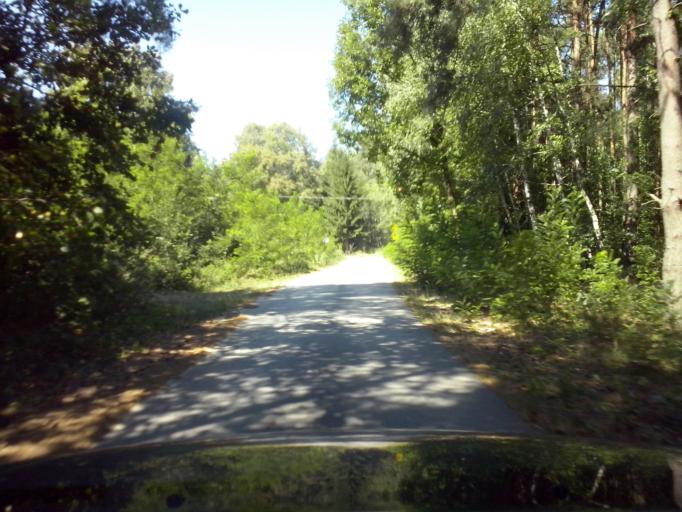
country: PL
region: Swietokrzyskie
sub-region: Powiat buski
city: Gnojno
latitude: 50.6321
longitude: 20.8659
